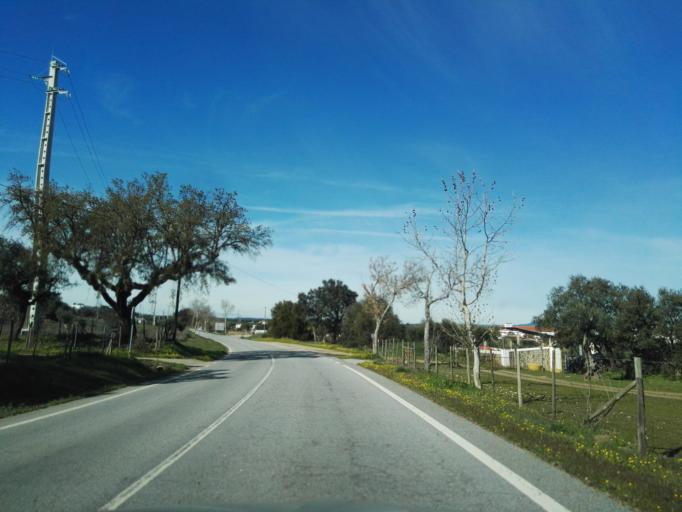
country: PT
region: Portalegre
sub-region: Arronches
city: Arronches
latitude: 39.1122
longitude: -7.2828
